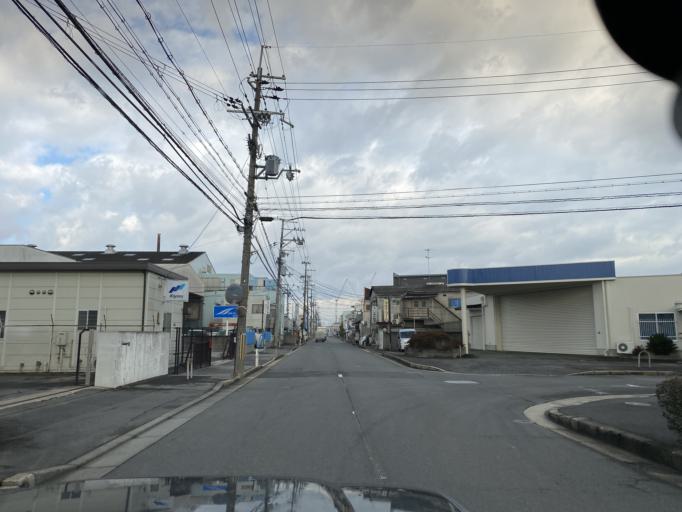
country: JP
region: Kyoto
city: Yawata
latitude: 34.8785
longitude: 135.7454
